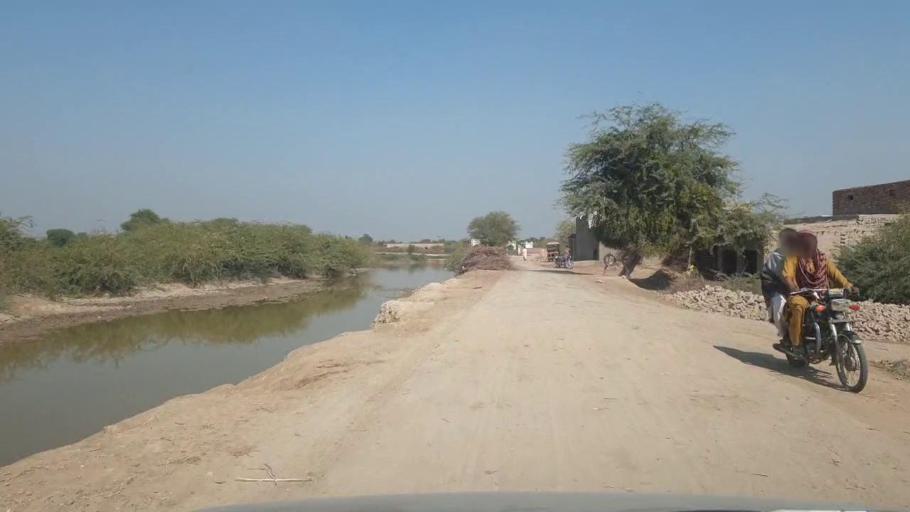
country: PK
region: Sindh
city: Chambar
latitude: 25.2432
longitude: 68.8610
